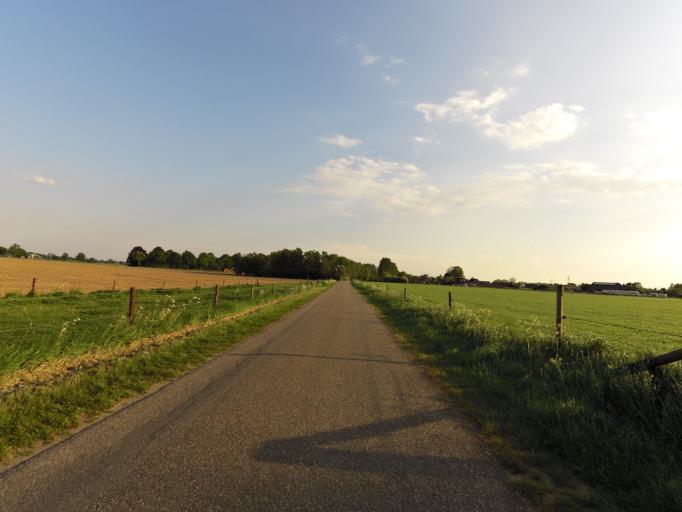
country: NL
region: Gelderland
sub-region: Oude IJsselstreek
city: Gendringen
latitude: 51.8649
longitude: 6.3582
